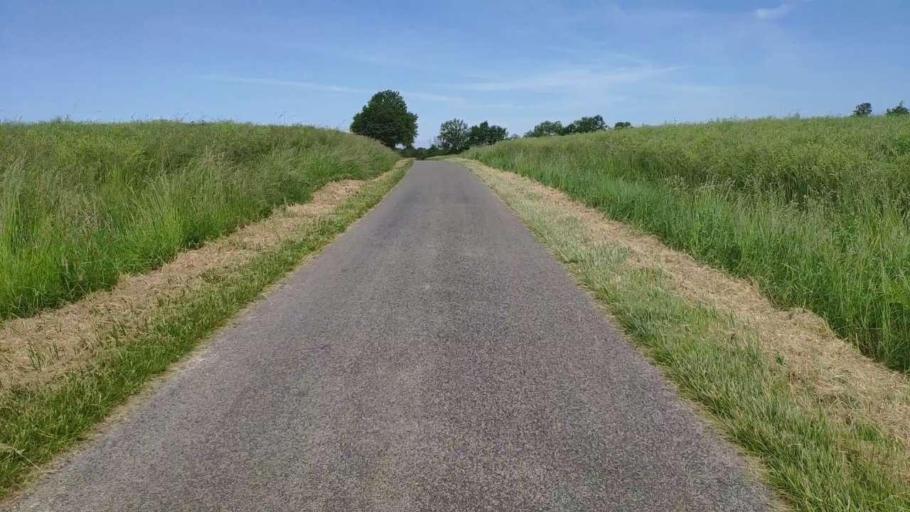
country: FR
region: Franche-Comte
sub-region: Departement du Jura
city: Bletterans
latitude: 46.6864
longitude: 5.4091
